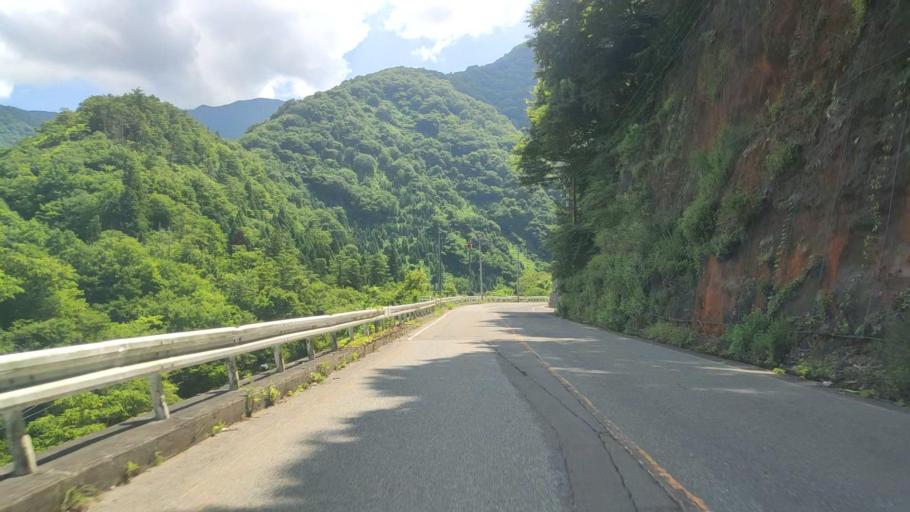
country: JP
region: Fukui
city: Ono
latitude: 35.9349
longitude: 136.5578
